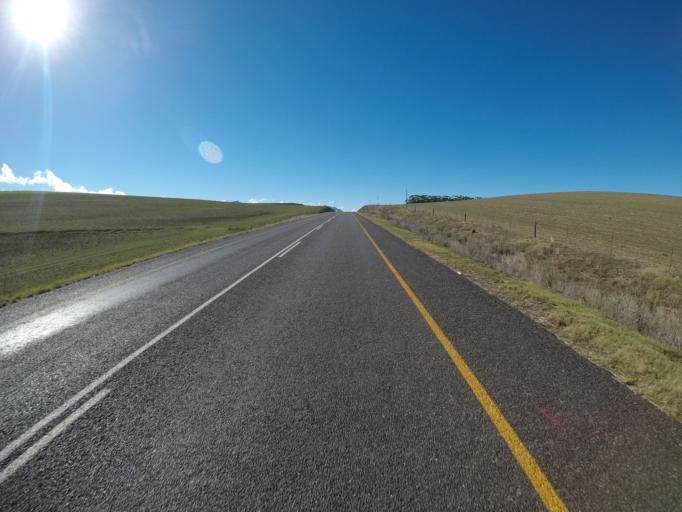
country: ZA
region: Western Cape
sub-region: Overberg District Municipality
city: Caledon
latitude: -34.1433
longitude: 19.4988
